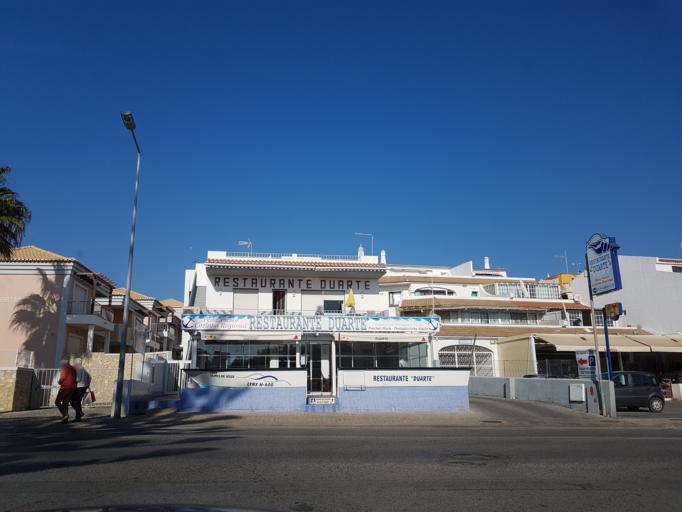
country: PT
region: Faro
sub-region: Loule
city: Boliqueime
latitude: 37.0932
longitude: -8.1908
